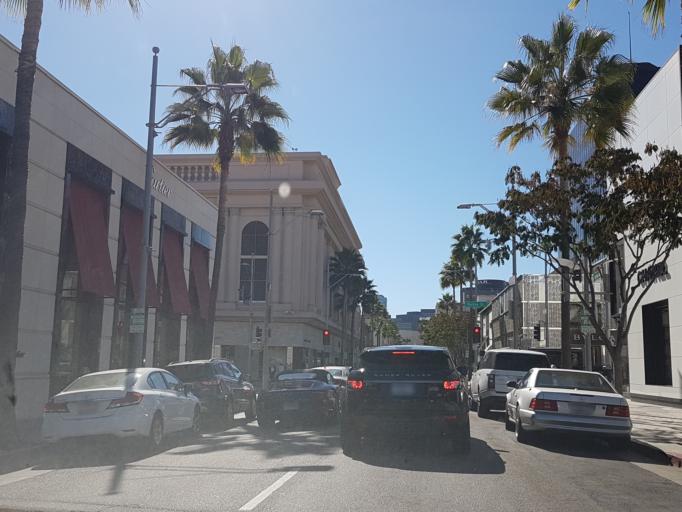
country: US
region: California
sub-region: Los Angeles County
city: Beverly Hills
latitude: 34.0695
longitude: -118.4026
